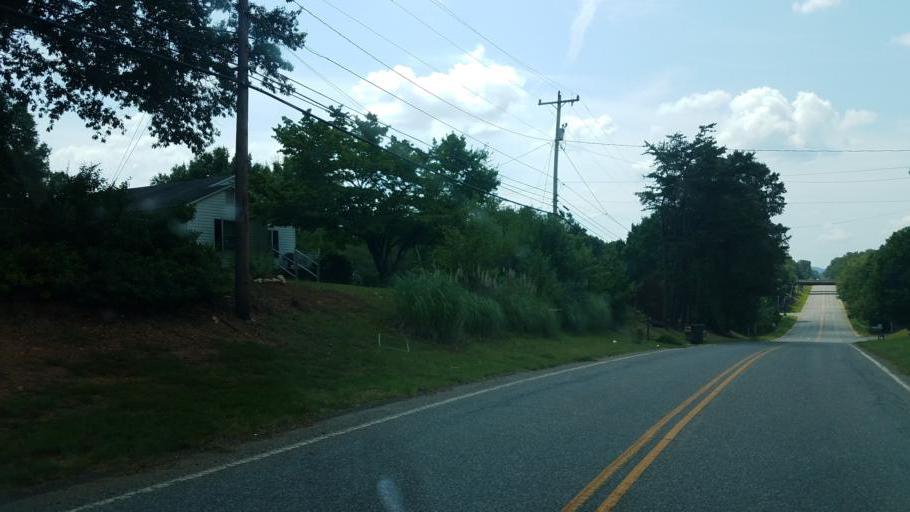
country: US
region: North Carolina
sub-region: Cleveland County
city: Kings Mountain
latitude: 35.2568
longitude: -81.3464
